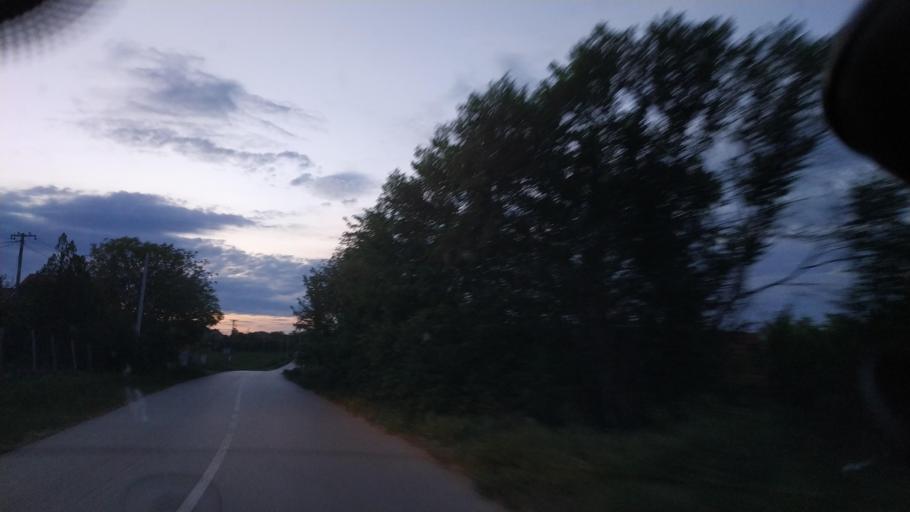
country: RS
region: Central Serbia
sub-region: Nisavski Okrug
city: Merosina
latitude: 43.3034
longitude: 21.6940
